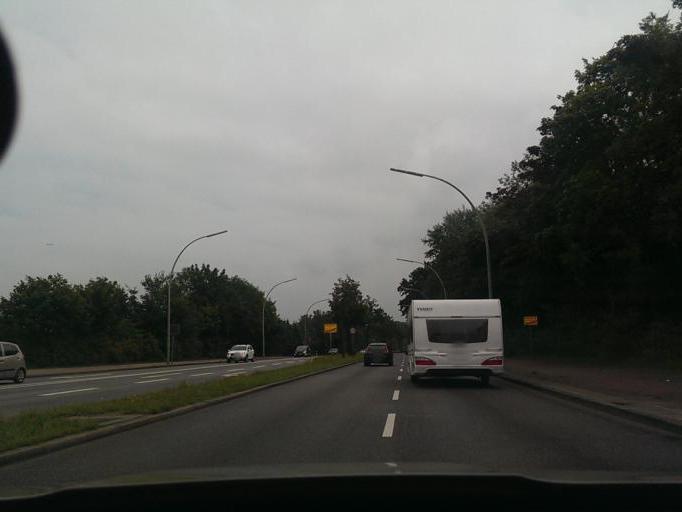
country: DE
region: Schleswig-Holstein
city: Bonningstedt
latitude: 53.6460
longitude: 9.9319
